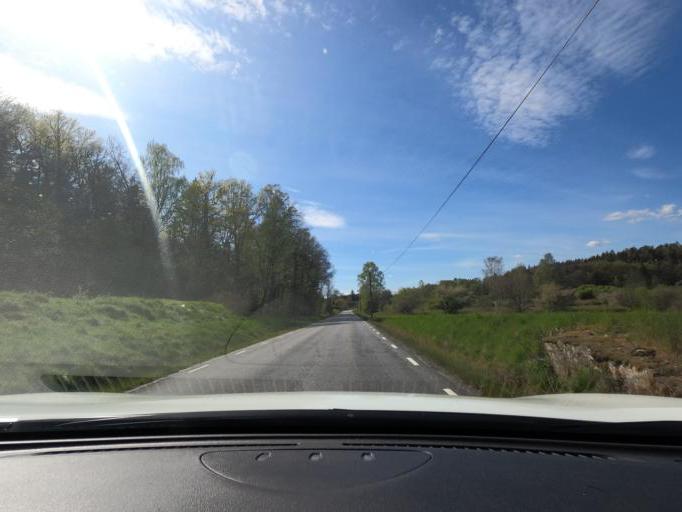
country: SE
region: Vaestra Goetaland
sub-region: Marks Kommun
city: Kinna
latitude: 57.4750
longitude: 12.5789
